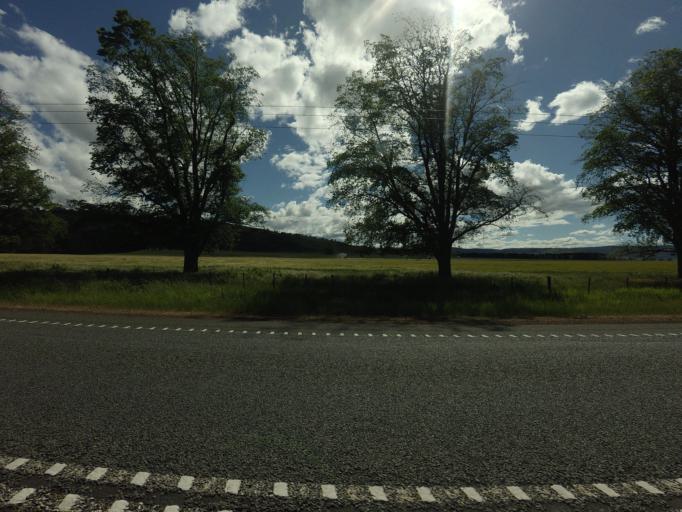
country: AU
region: Tasmania
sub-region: Northern Midlands
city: Evandale
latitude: -42.0408
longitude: 147.4829
